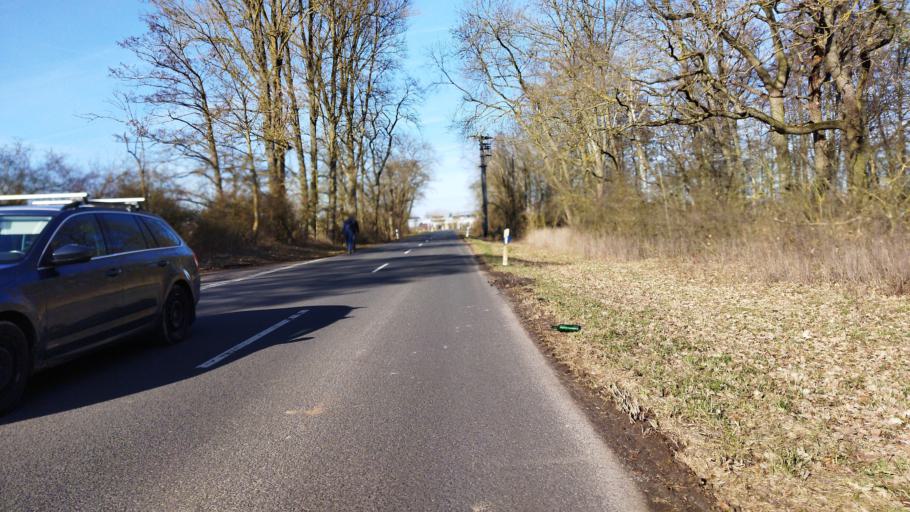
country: DE
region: Bavaria
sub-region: Regierungsbezirk Unterfranken
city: Grafenrheinfeld
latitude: 49.9901
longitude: 10.1997
